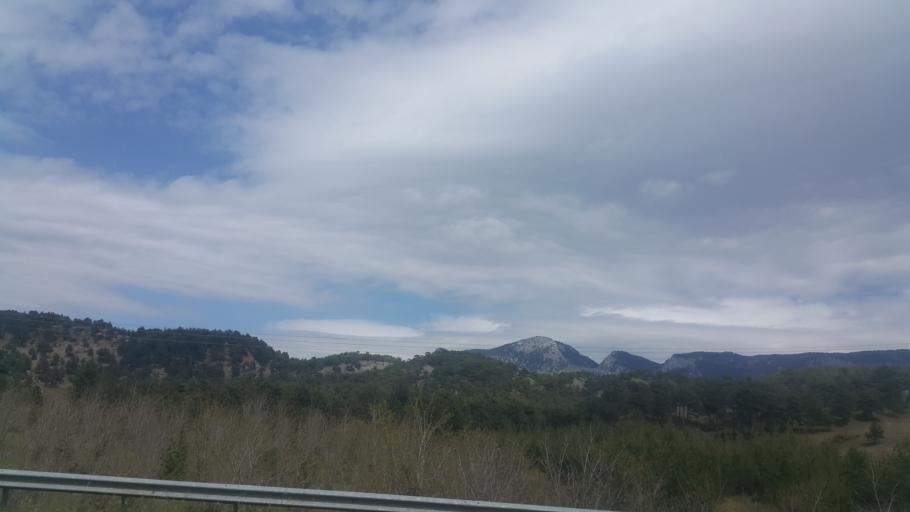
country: TR
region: Adana
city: Pozanti
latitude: 37.4571
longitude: 34.8797
